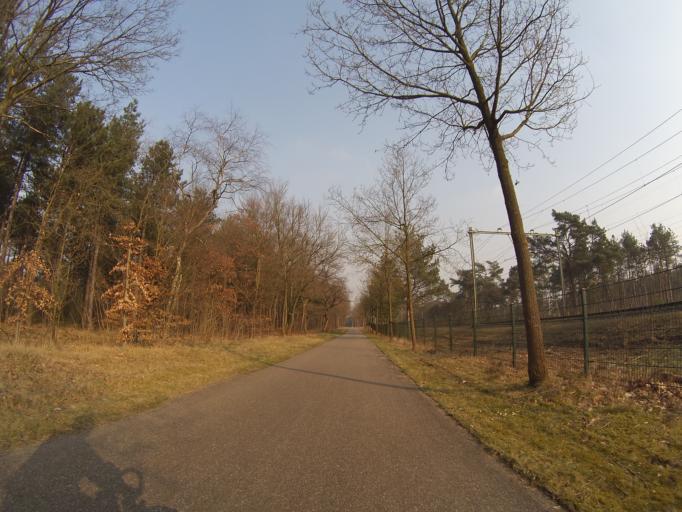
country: NL
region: Utrecht
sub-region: Gemeente Soest
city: Soest
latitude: 52.1446
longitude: 5.3129
